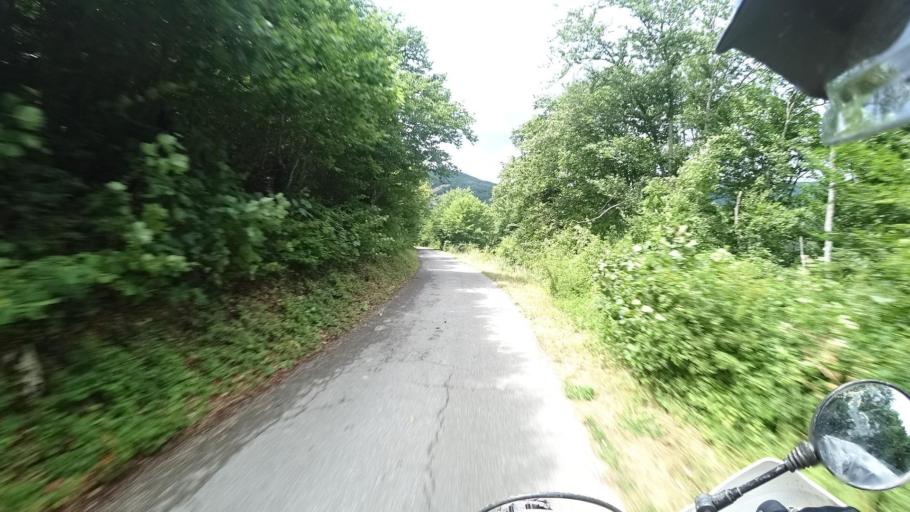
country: HR
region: Licko-Senjska
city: Jezerce
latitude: 44.7431
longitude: 15.4995
